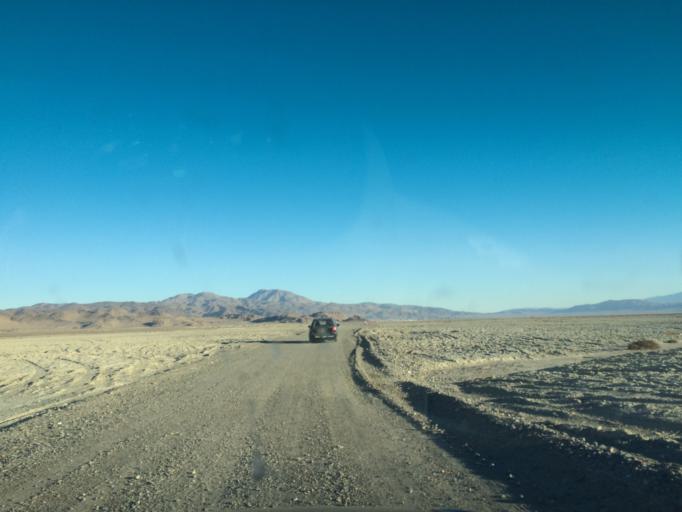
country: US
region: California
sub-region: San Bernardino County
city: Searles Valley
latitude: 35.6535
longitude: -117.3775
